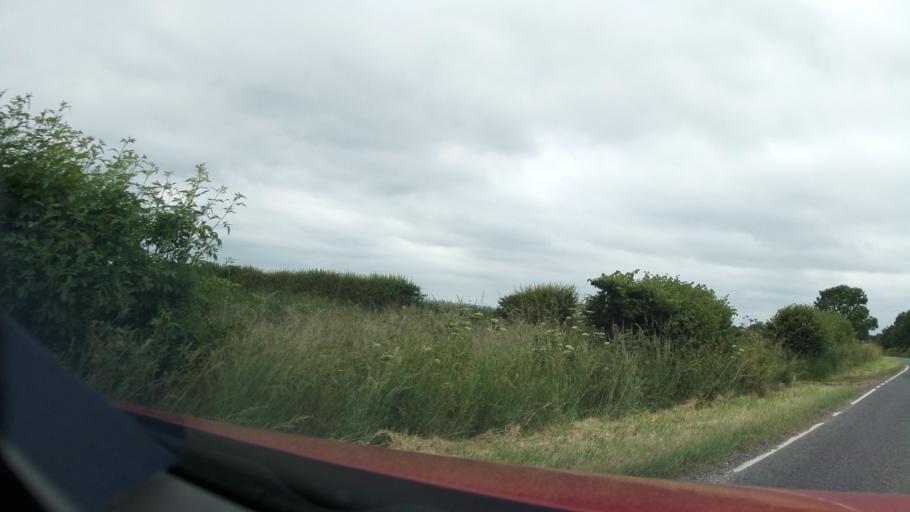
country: GB
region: England
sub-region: Nottinghamshire
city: East Leake
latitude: 52.8127
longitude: -1.1319
